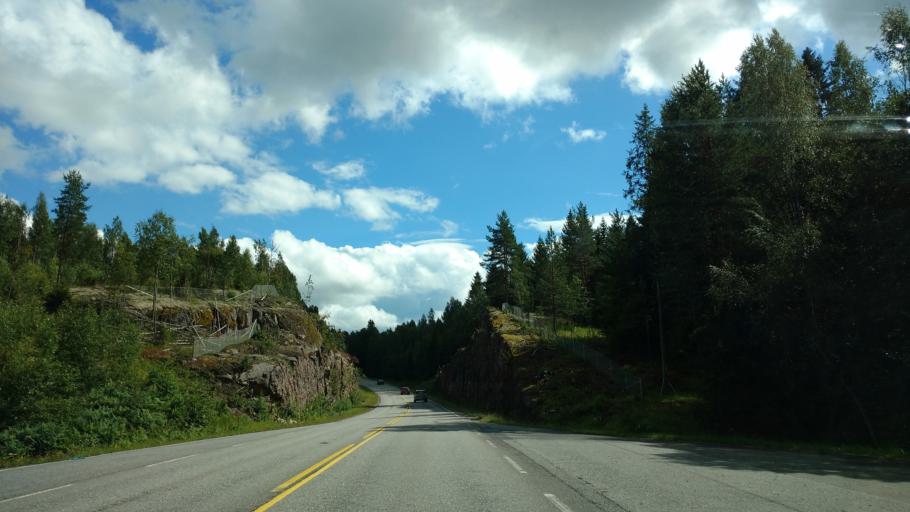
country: FI
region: Uusimaa
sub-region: Helsinki
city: Karjalohja
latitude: 60.2134
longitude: 23.6454
